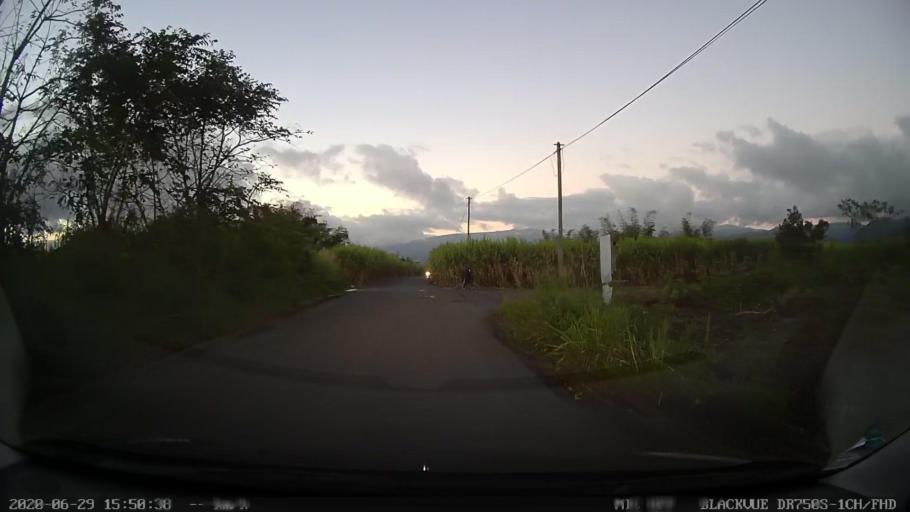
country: RE
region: Reunion
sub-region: Reunion
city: Bras-Panon
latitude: -20.9904
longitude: 55.6927
